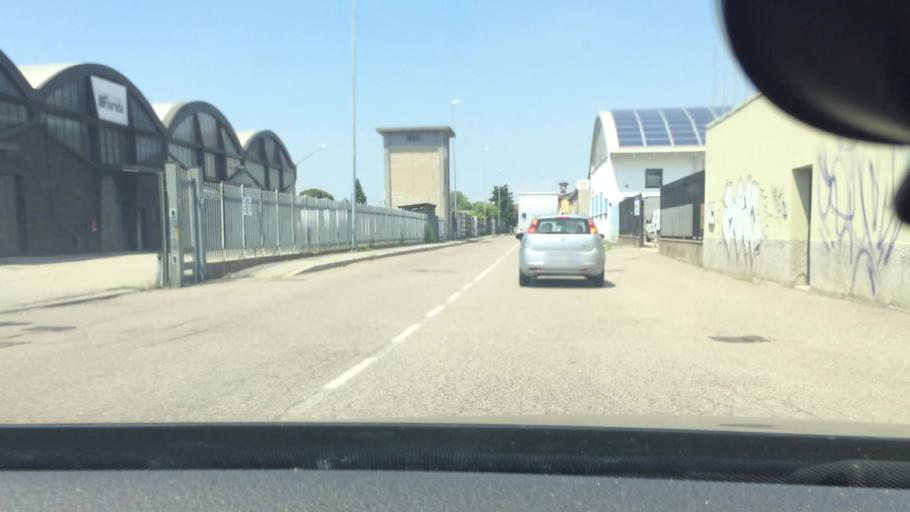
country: IT
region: Lombardy
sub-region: Citta metropolitana di Milano
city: Pero
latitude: 45.5039
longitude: 9.0871
